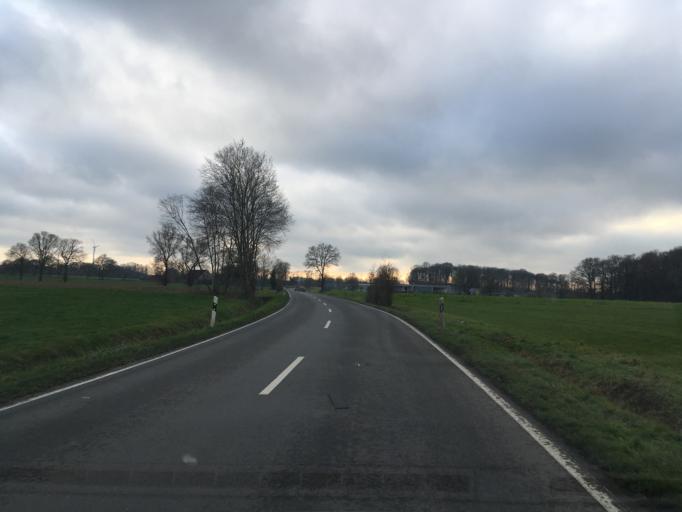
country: DE
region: North Rhine-Westphalia
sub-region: Regierungsbezirk Munster
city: Gescher
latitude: 51.9443
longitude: 6.9551
